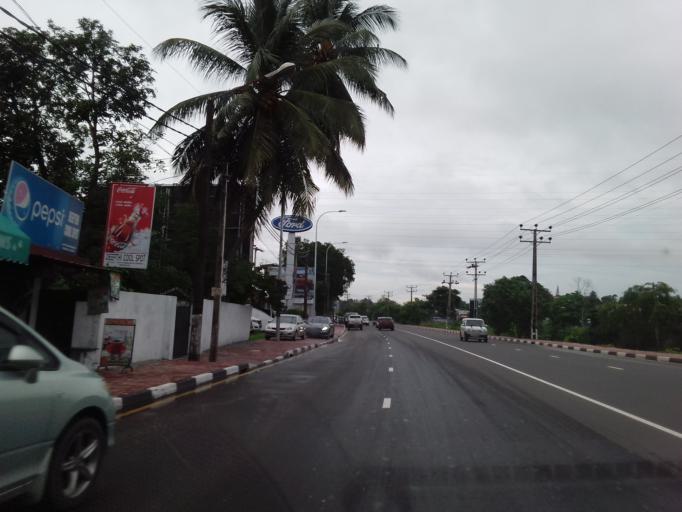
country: LK
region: Western
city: Battaramulla South
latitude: 6.8931
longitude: 79.9225
